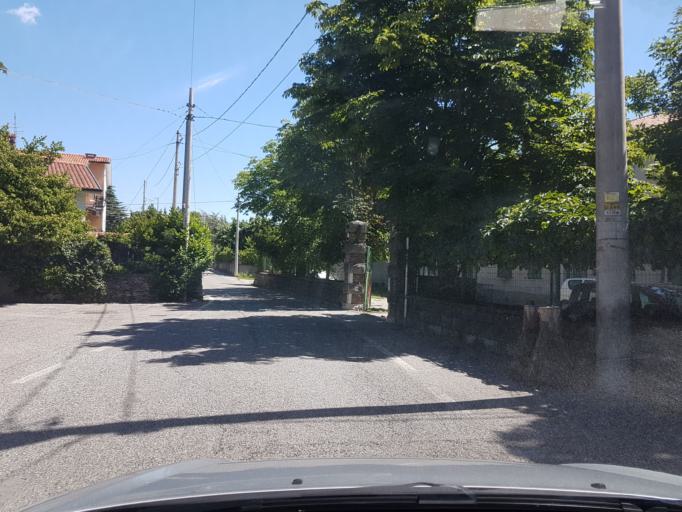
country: IT
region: Friuli Venezia Giulia
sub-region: Provincia di Trieste
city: Villa Opicina
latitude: 45.6913
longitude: 13.7915
